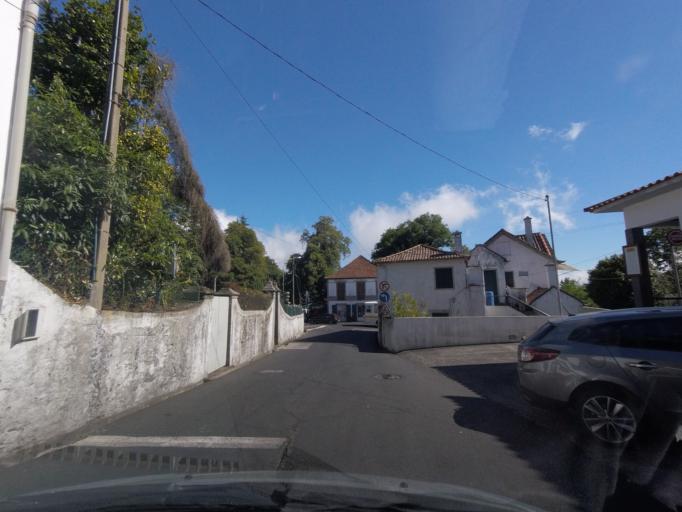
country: PT
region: Madeira
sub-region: Santa Cruz
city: Camacha
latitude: 32.6804
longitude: -16.8458
